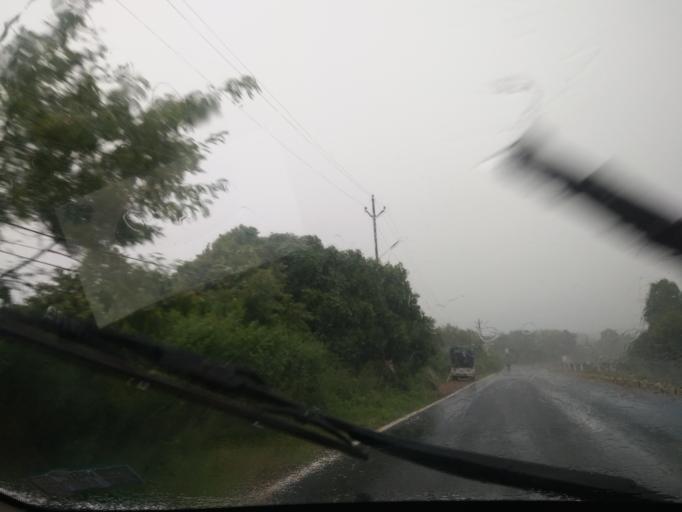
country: IN
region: Goa
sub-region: North Goa
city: Bambolim
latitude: 15.4660
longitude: 73.8517
